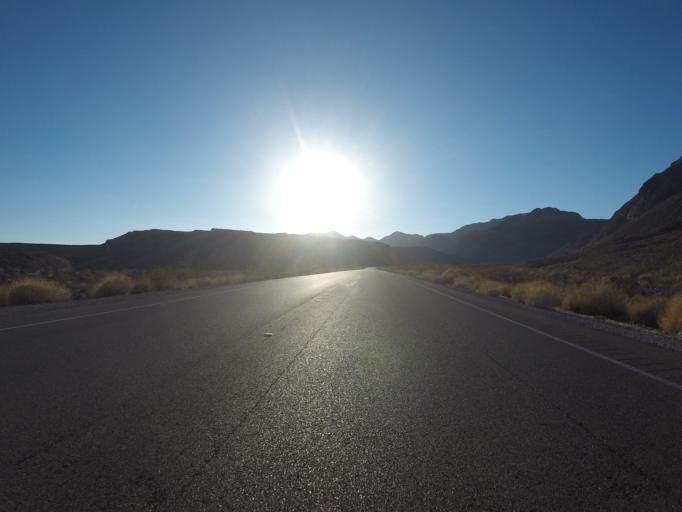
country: US
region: Nevada
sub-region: Clark County
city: Moapa Valley
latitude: 36.3643
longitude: -114.4655
